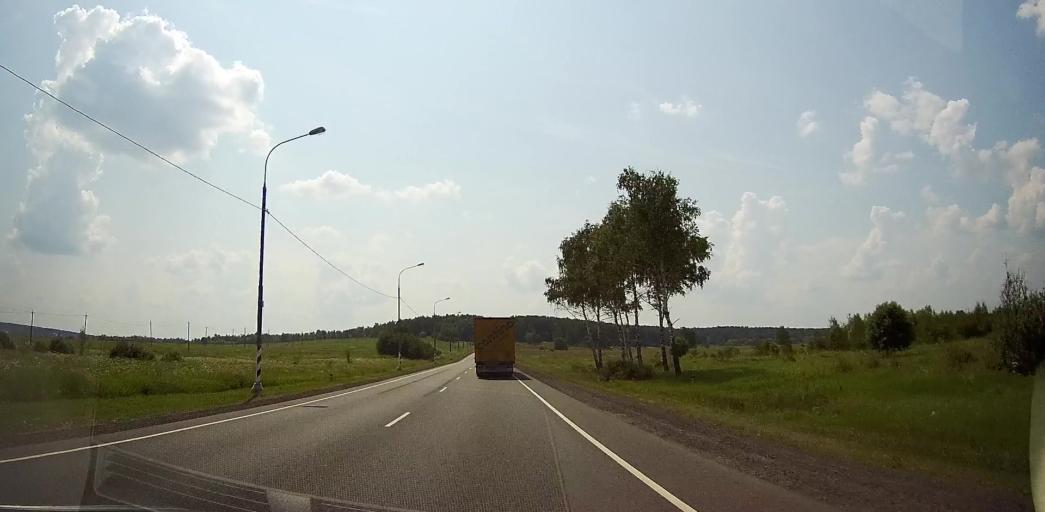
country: RU
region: Moskovskaya
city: Meshcherino
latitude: 55.1862
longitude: 38.3562
